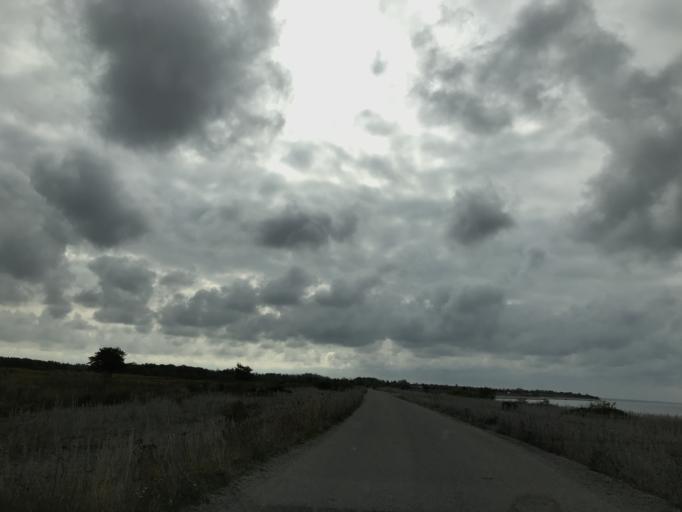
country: SE
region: Kalmar
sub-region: Borgholms Kommun
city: Borgholm
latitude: 57.0541
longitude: 16.8365
